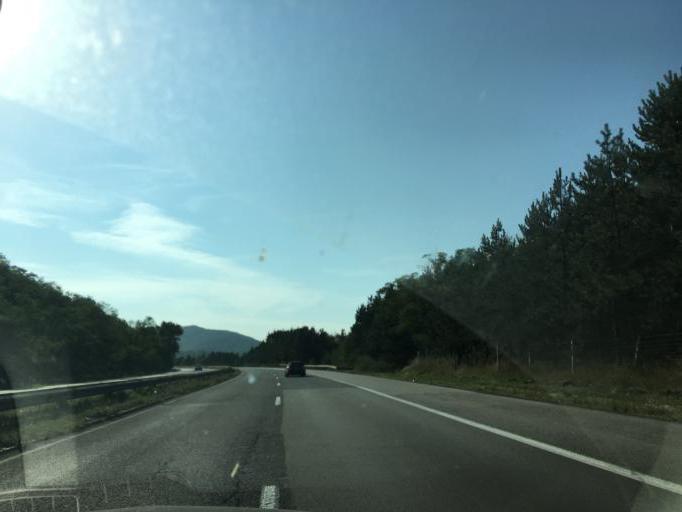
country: BG
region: Sofiya
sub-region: Obshtina Ikhtiman
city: Ikhtiman
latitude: 42.3758
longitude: 23.8789
